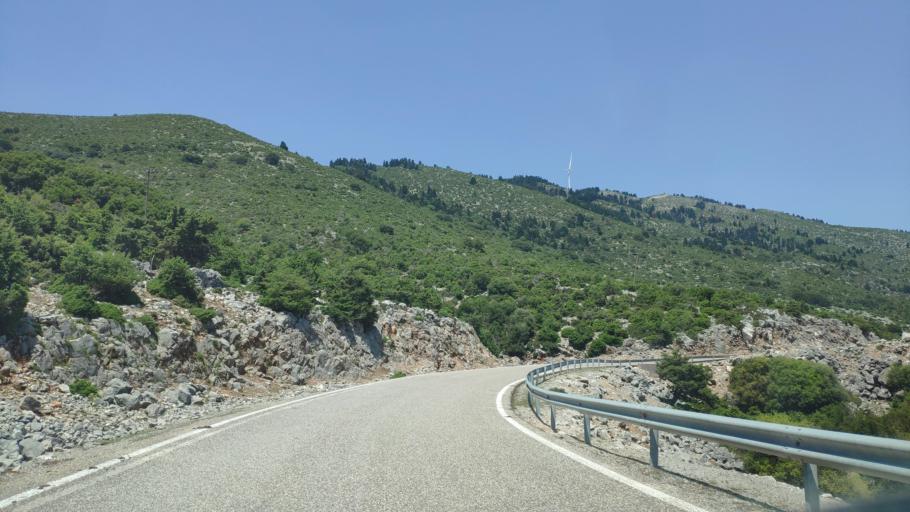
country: GR
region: West Greece
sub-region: Nomos Aitolias kai Akarnanias
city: Krikellos
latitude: 39.0582
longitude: 21.3845
